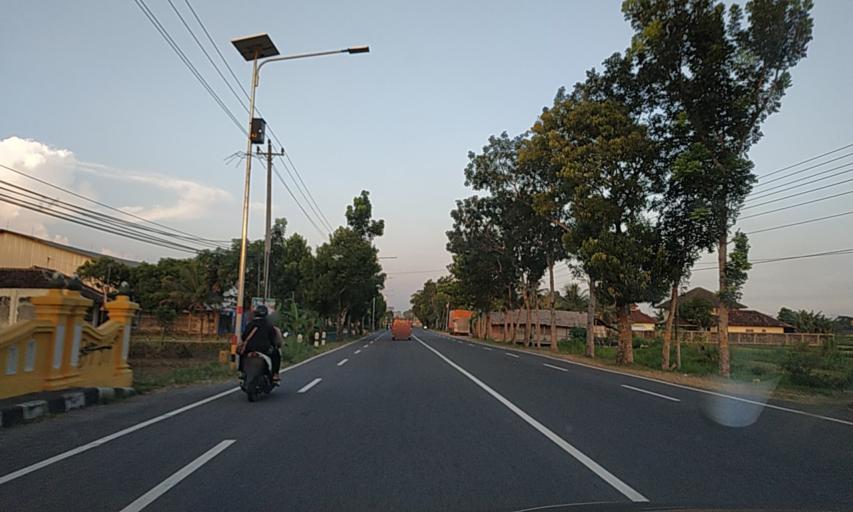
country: ID
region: Daerah Istimewa Yogyakarta
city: Srandakan
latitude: -7.8909
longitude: 110.1187
